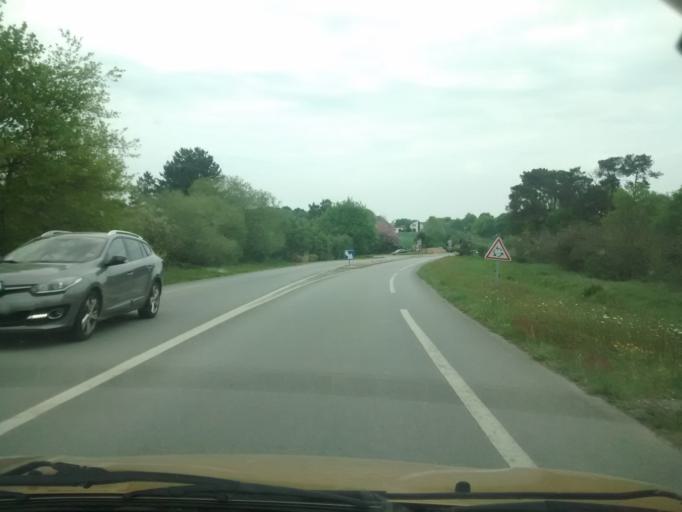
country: FR
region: Brittany
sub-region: Departement du Morbihan
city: Berric
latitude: 47.6137
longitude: -2.5405
